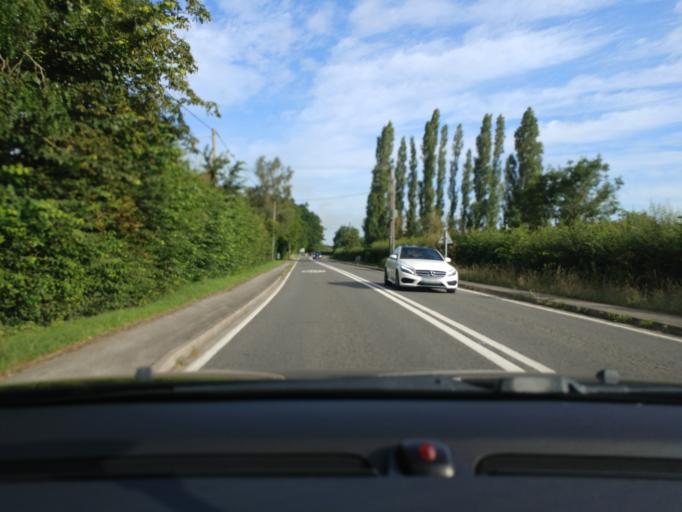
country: GB
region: England
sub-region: Oxfordshire
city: Kidlington
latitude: 51.8603
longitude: -1.2229
